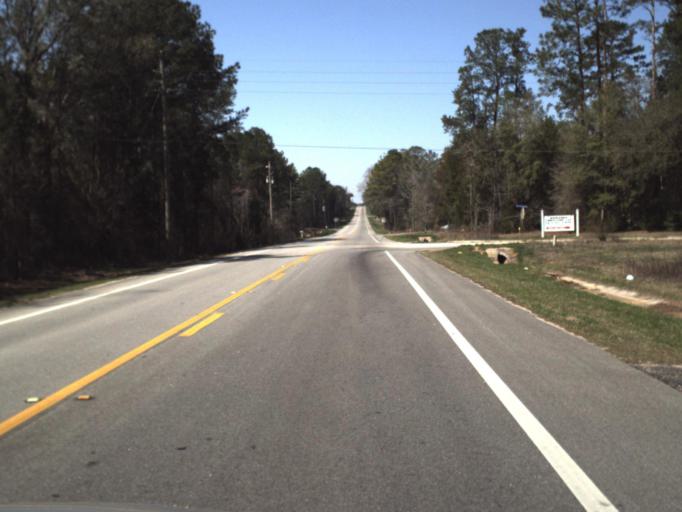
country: US
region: Florida
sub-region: Jackson County
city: Marianna
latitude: 30.7906
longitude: -85.2629
